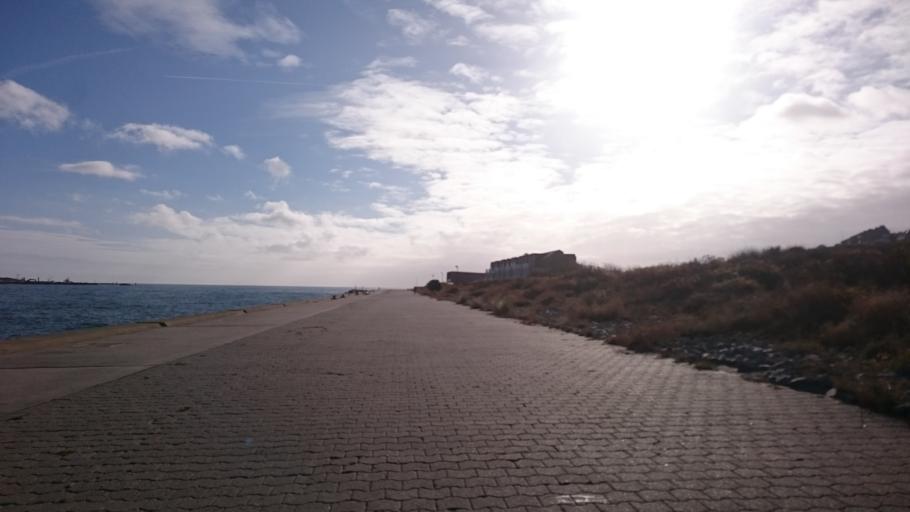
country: DE
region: Schleswig-Holstein
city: Helgoland
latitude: 54.1872
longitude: 7.8866
